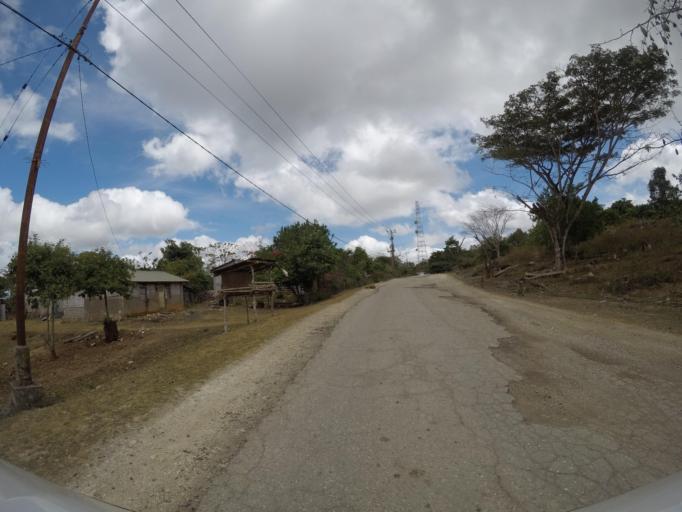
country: TL
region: Lautem
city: Lospalos
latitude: -8.4416
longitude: 126.9638
